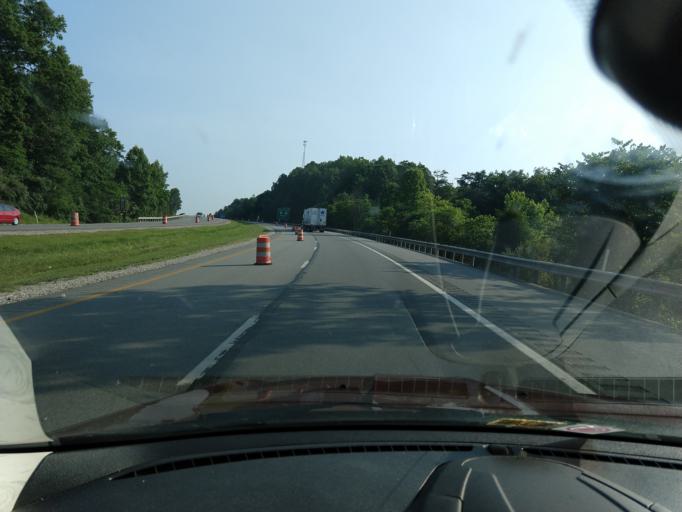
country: US
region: West Virginia
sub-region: Jackson County
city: Ripley
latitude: 38.8019
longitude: -81.7284
